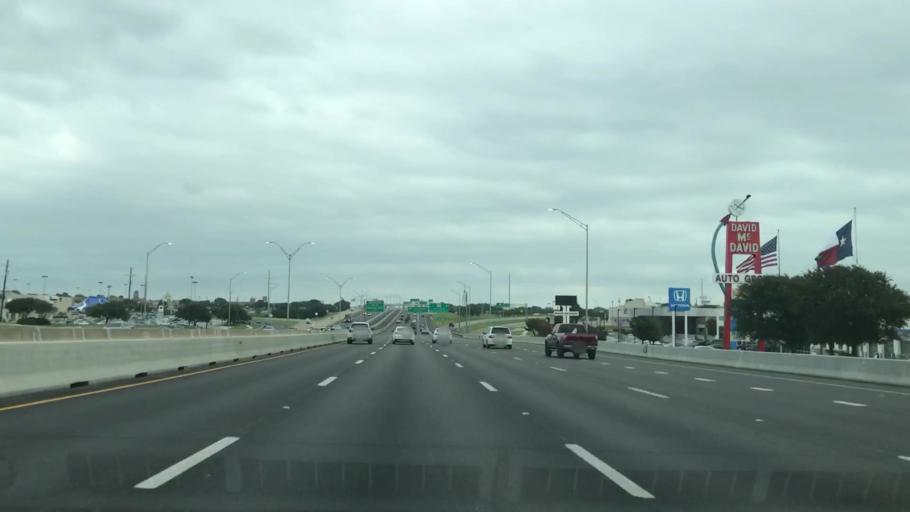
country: US
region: Texas
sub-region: Dallas County
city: Irving
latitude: 32.8369
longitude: -97.0016
